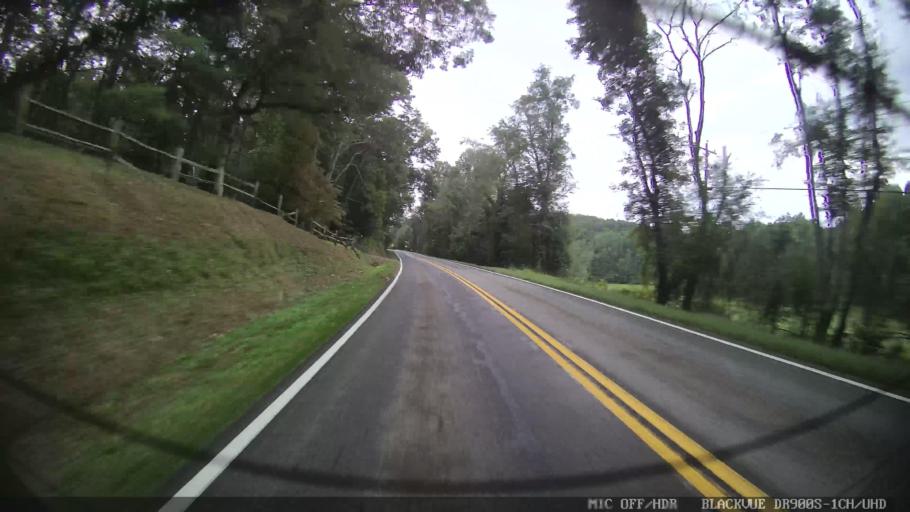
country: US
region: Georgia
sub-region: Gilmer County
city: Ellijay
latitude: 34.7104
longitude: -84.4974
